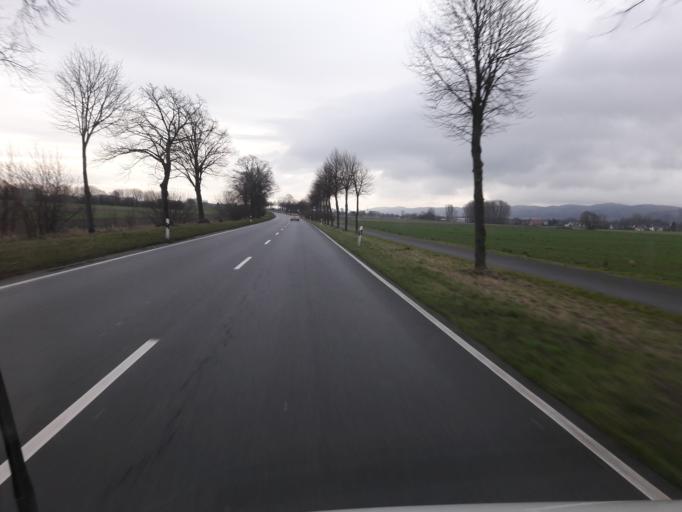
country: DE
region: North Rhine-Westphalia
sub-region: Regierungsbezirk Detmold
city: Hille
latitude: 52.3009
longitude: 8.7430
